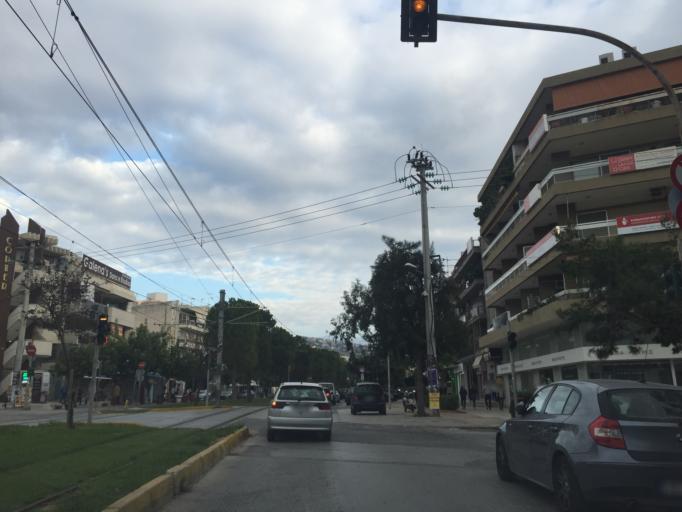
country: GR
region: Attica
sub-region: Nomarchia Athinas
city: Glyfada
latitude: 37.8633
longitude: 23.7489
